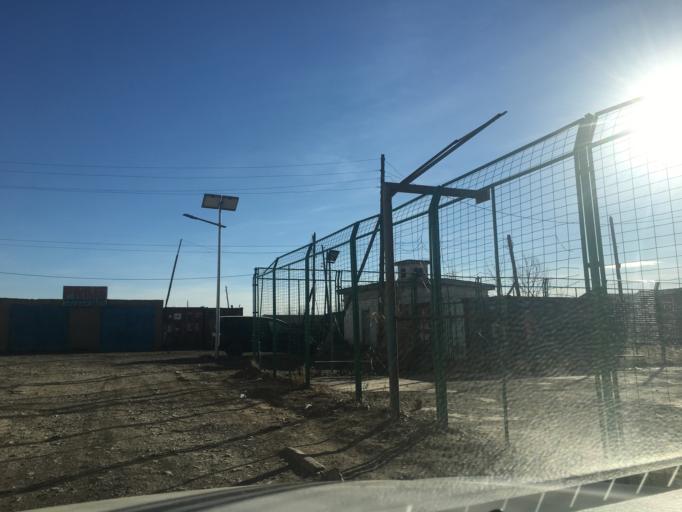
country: MN
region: Ulaanbaatar
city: Ulaanbaatar
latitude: 47.9074
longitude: 106.7966
